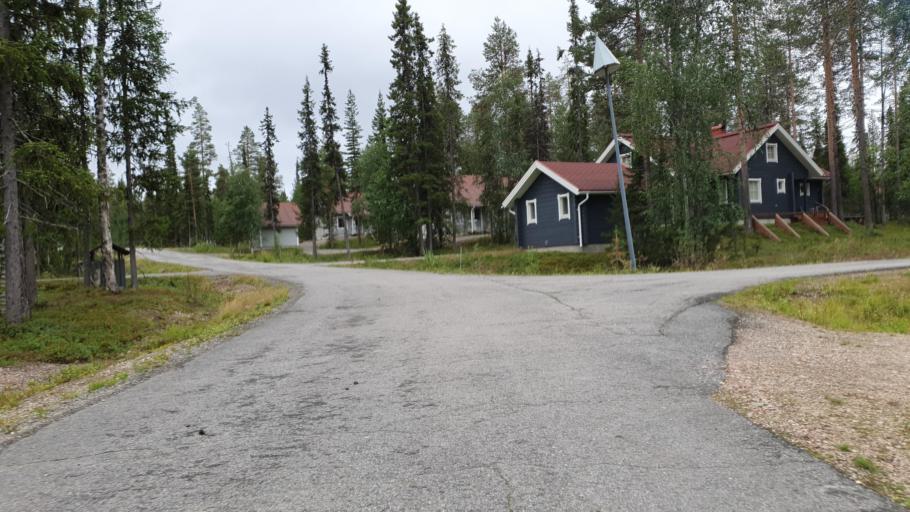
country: FI
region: Lapland
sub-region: Tunturi-Lappi
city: Kolari
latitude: 67.6000
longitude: 24.1816
